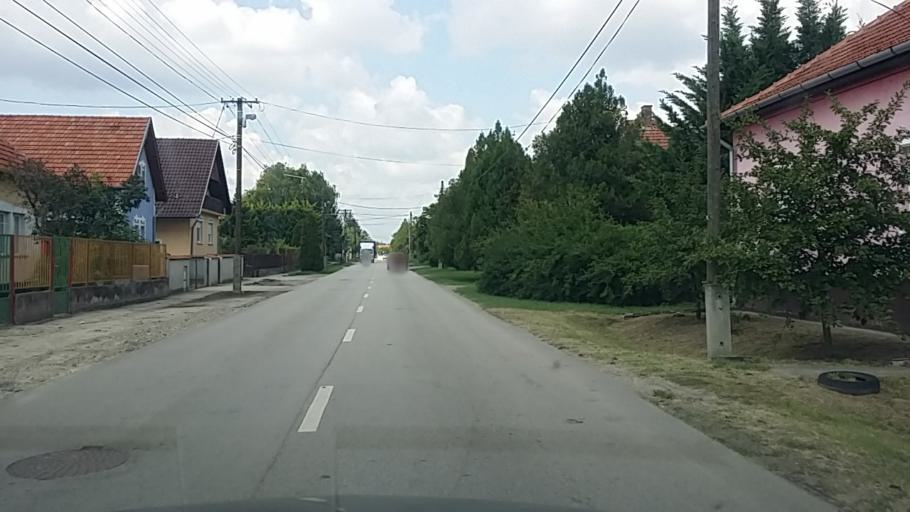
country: HU
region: Bacs-Kiskun
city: Tiszaalpar
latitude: 46.8089
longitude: 20.0037
